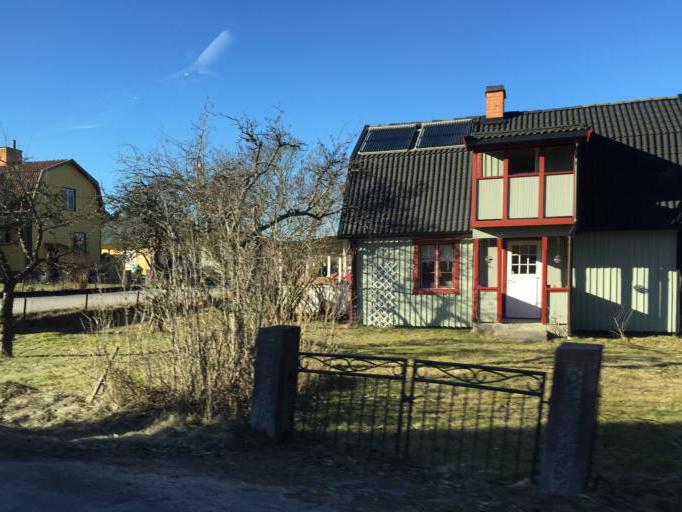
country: SE
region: Soedermanland
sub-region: Vingakers Kommun
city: Vingaker
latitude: 59.0345
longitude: 15.8488
